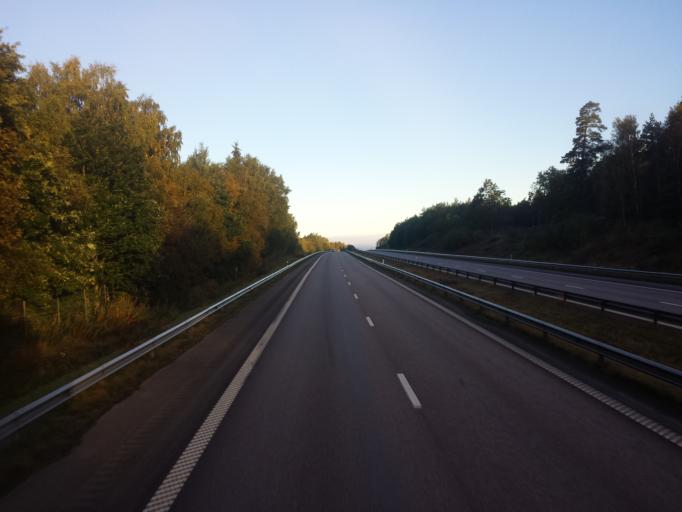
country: SE
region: Halland
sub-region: Kungsbacka Kommun
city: Kungsbacka
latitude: 57.4456
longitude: 12.1071
